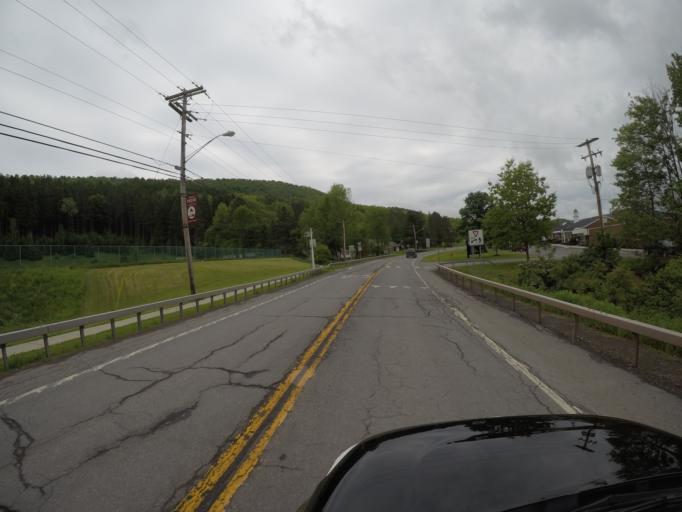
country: US
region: New York
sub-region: Delaware County
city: Delhi
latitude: 42.2690
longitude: -74.9155
